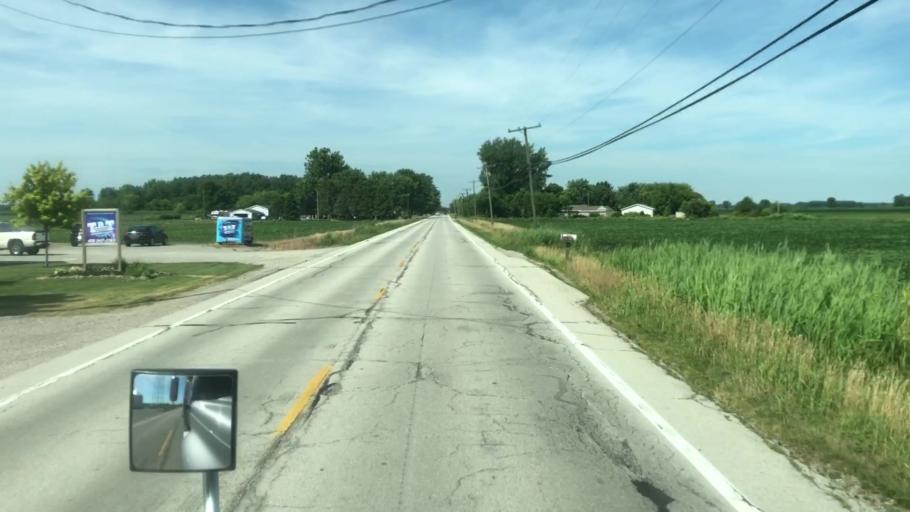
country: US
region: Ohio
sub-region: Ottawa County
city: Port Clinton
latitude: 41.4131
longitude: -82.9031
